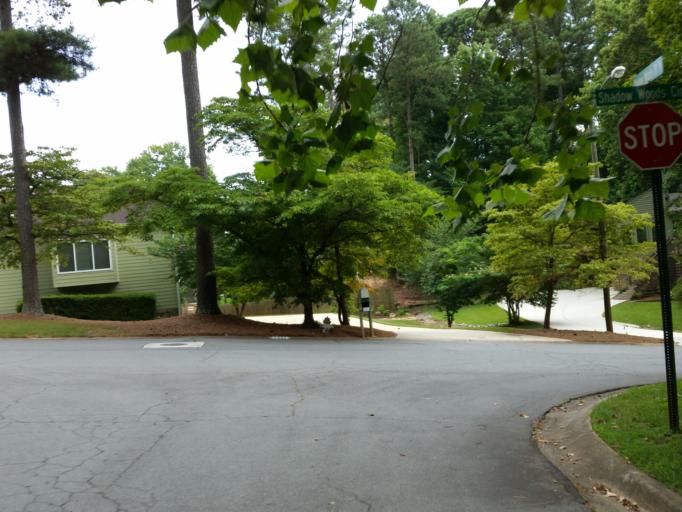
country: US
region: Georgia
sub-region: Cobb County
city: Marietta
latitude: 34.0005
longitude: -84.4758
